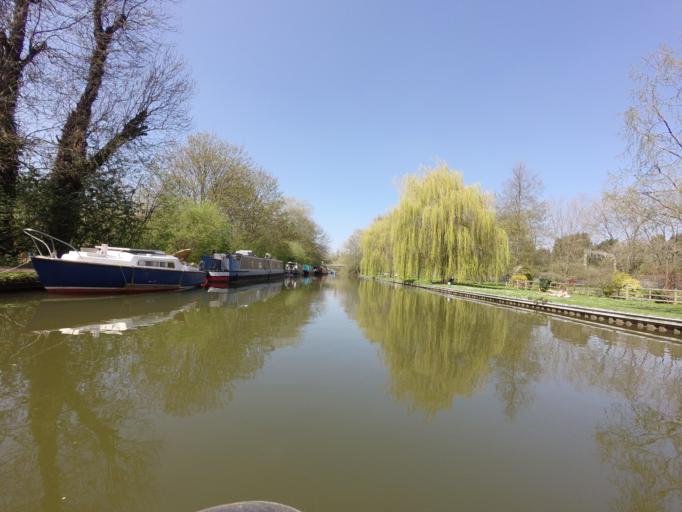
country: GB
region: England
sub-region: Hertfordshire
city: Berkhamsted
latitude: 51.7635
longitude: -0.5689
